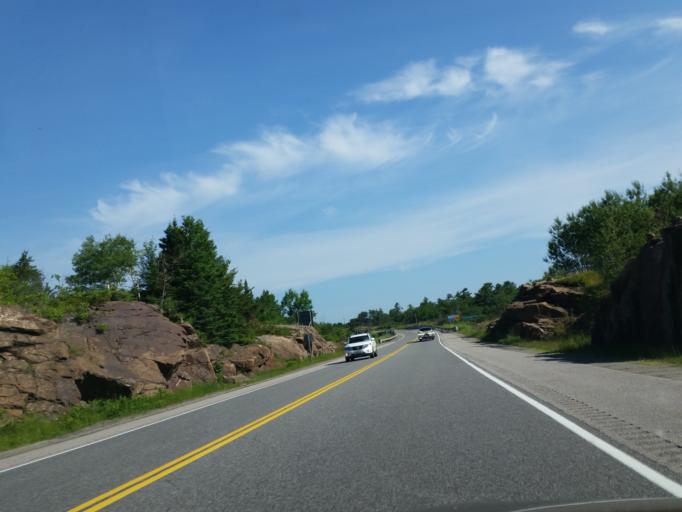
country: CA
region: Ontario
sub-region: Parry Sound District
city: Parry Sound
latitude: 45.7724
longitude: -80.4968
